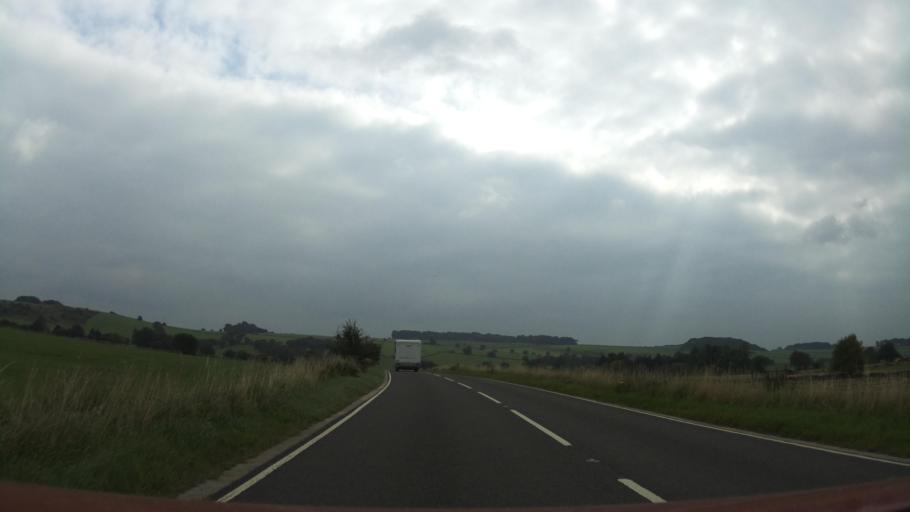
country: GB
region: England
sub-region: Staffordshire
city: Mayfield
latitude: 53.0297
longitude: -1.8356
